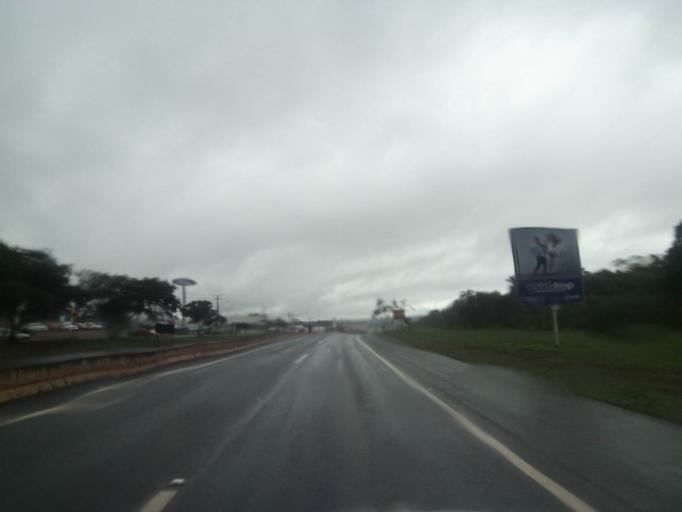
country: PY
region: Alto Parana
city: Ciudad del Este
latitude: -25.5093
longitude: -54.5783
